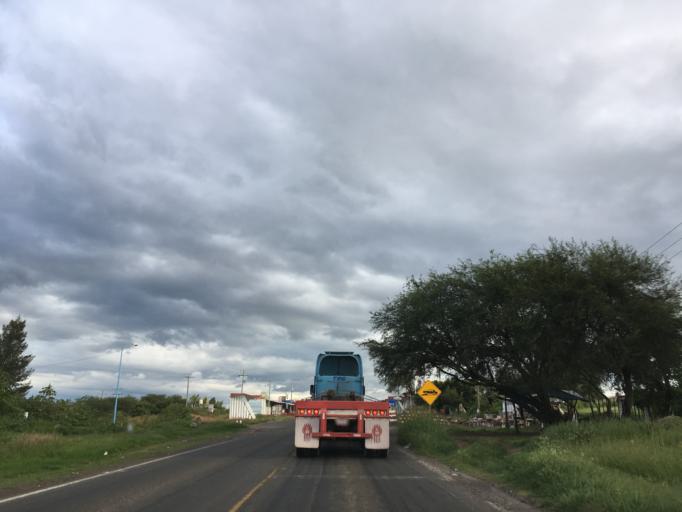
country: MX
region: Michoacan
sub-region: Cuitzeo
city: Cuamio
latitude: 20.0619
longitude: -101.1516
